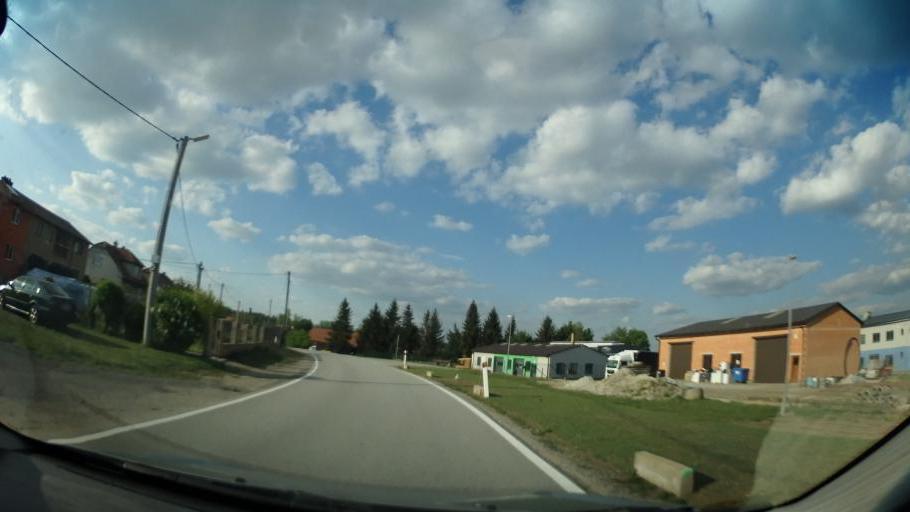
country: CZ
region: Vysocina
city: Merin
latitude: 49.3604
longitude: 15.9080
